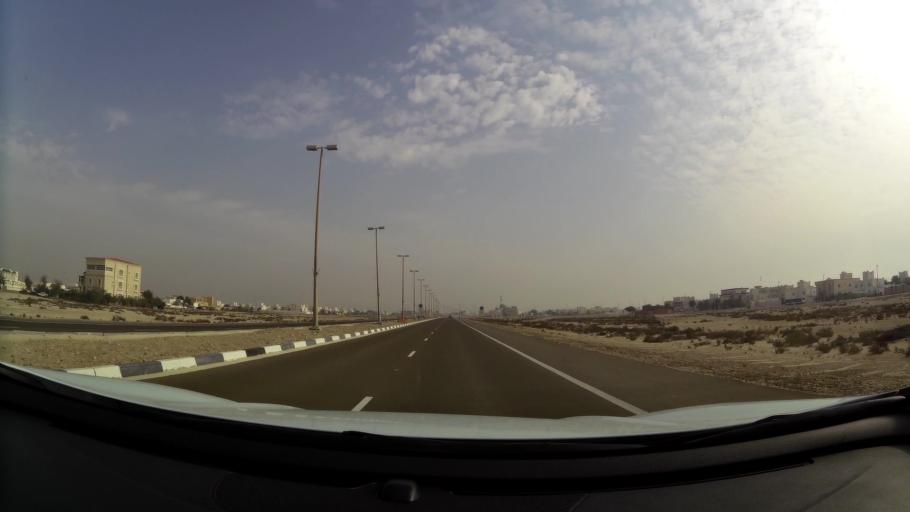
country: AE
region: Abu Dhabi
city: Abu Dhabi
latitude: 24.6636
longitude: 54.7673
